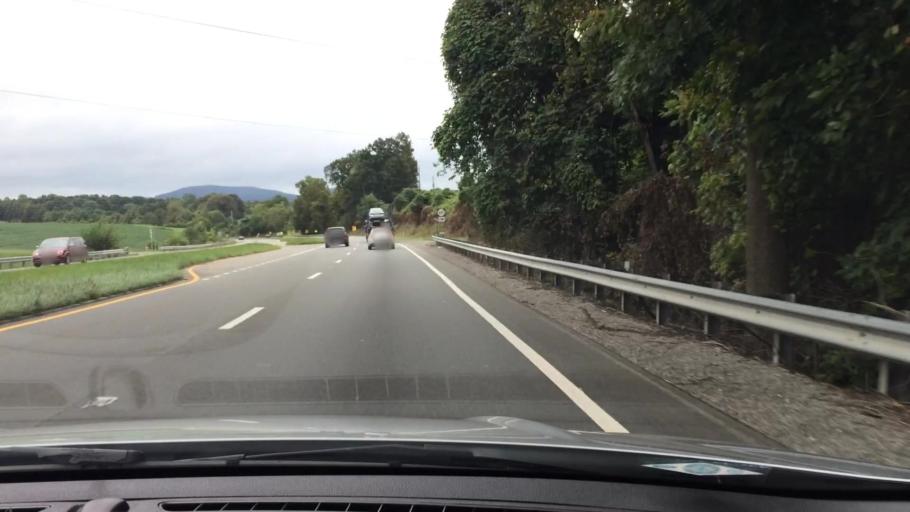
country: US
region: Virginia
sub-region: Franklin County
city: Rocky Mount
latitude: 37.0952
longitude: -79.9393
